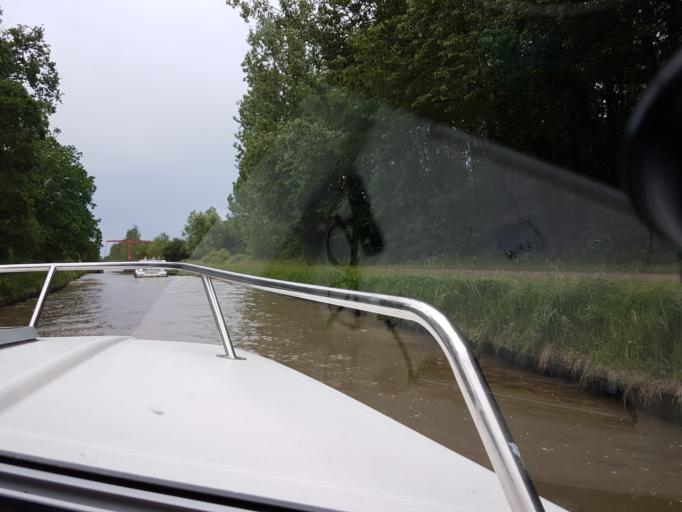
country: FR
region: Bourgogne
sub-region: Departement de la Nievre
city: Clamecy
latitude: 47.3897
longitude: 3.5988
